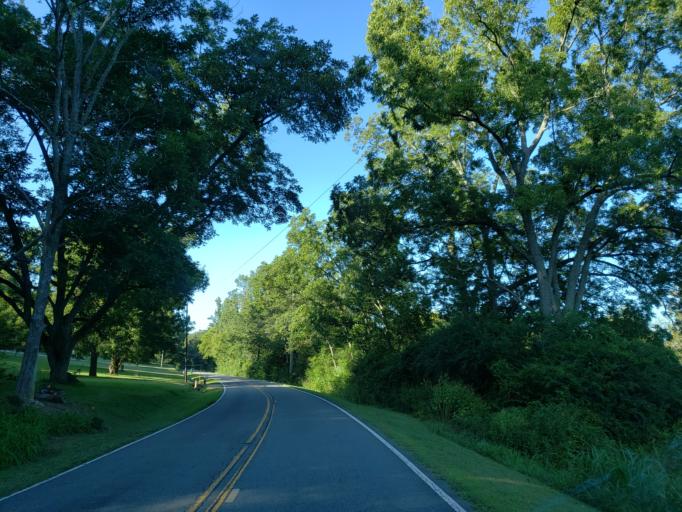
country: US
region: Georgia
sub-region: Bartow County
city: Rydal
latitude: 34.3106
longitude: -84.7576
